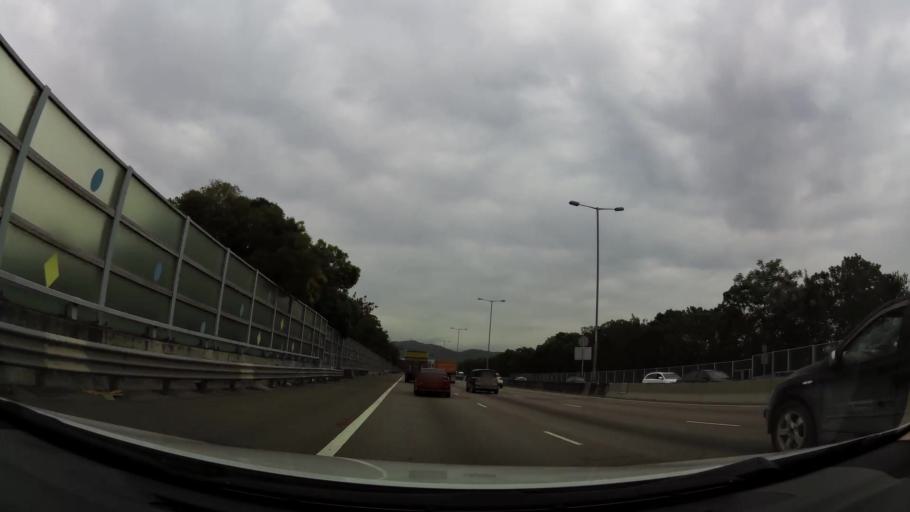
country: HK
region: Yuen Long
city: Yuen Long Kau Hui
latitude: 22.4350
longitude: 114.0251
